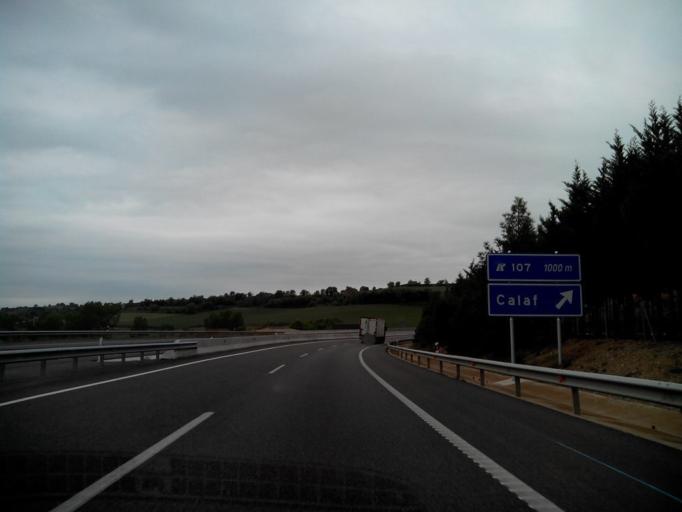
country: ES
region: Catalonia
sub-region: Provincia de Barcelona
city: Calaf
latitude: 41.7313
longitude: 1.5509
